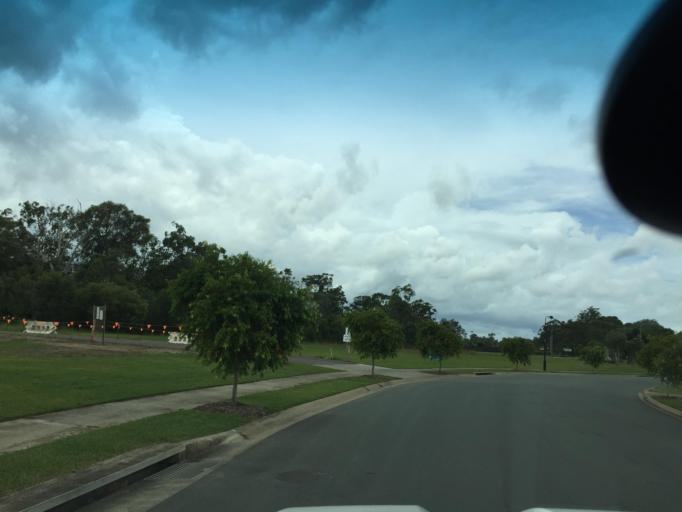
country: AU
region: Queensland
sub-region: Moreton Bay
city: Caboolture
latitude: -27.0606
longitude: 152.9308
